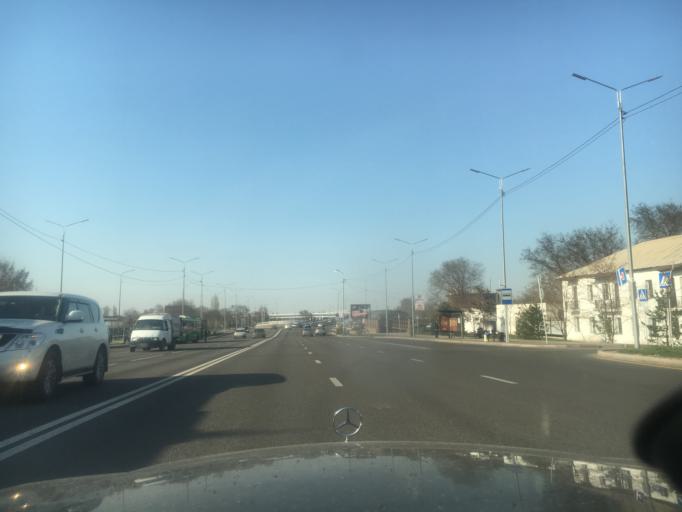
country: KZ
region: Almaty Qalasy
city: Almaty
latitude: 43.2709
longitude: 76.9448
